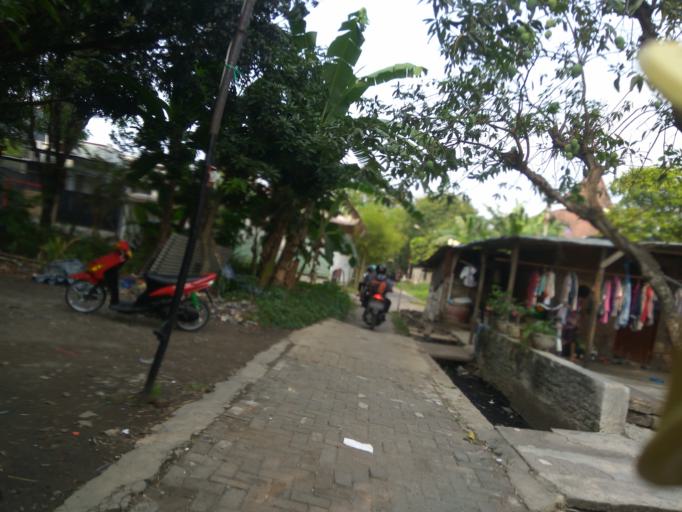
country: ID
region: Central Java
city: Semarang
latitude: -6.9703
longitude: 110.3957
